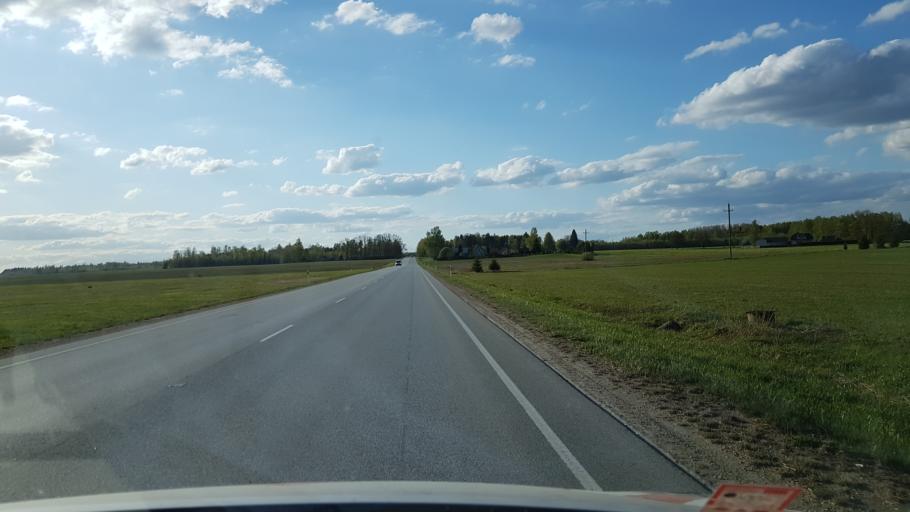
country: EE
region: Vorumaa
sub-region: Voru linn
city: Voru
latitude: 57.9105
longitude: 26.8245
